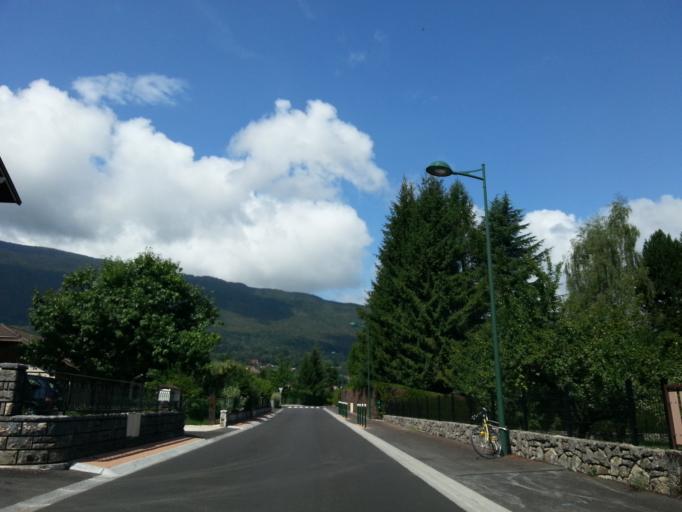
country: FR
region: Rhone-Alpes
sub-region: Departement de la Haute-Savoie
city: Saint-Jorioz
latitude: 45.8280
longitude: 6.1645
